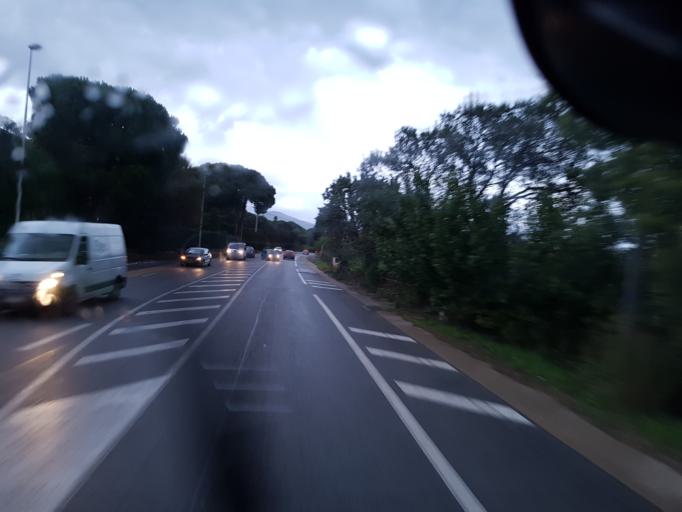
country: FR
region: Provence-Alpes-Cote d'Azur
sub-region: Departement du Var
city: Gassin
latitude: 43.2543
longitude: 6.5747
